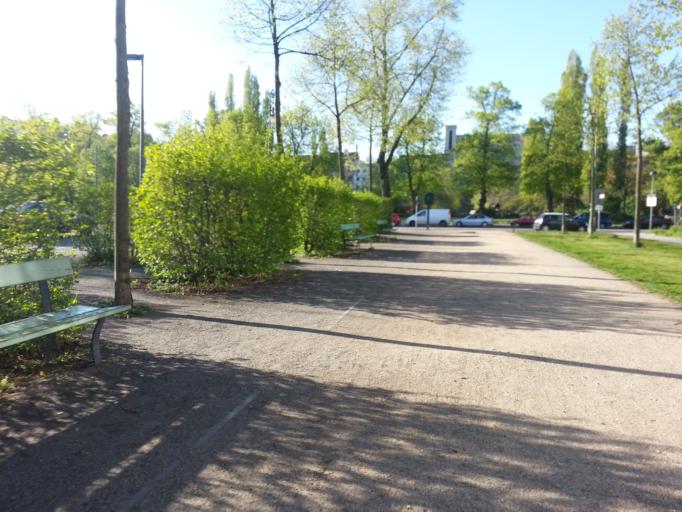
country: DE
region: Berlin
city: Charlottenburg Bezirk
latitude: 52.5196
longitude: 13.2911
